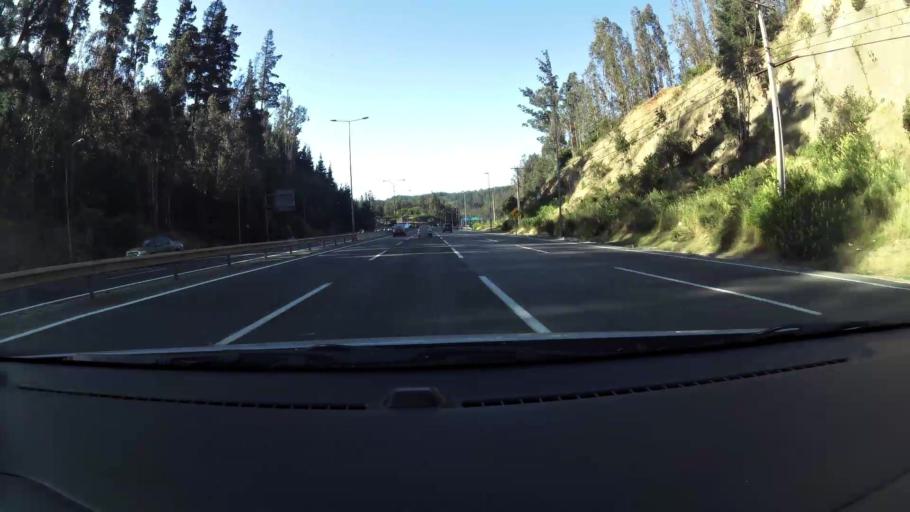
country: CL
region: Valparaiso
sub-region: Provincia de Valparaiso
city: Vina del Mar
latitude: -33.1023
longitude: -71.5480
